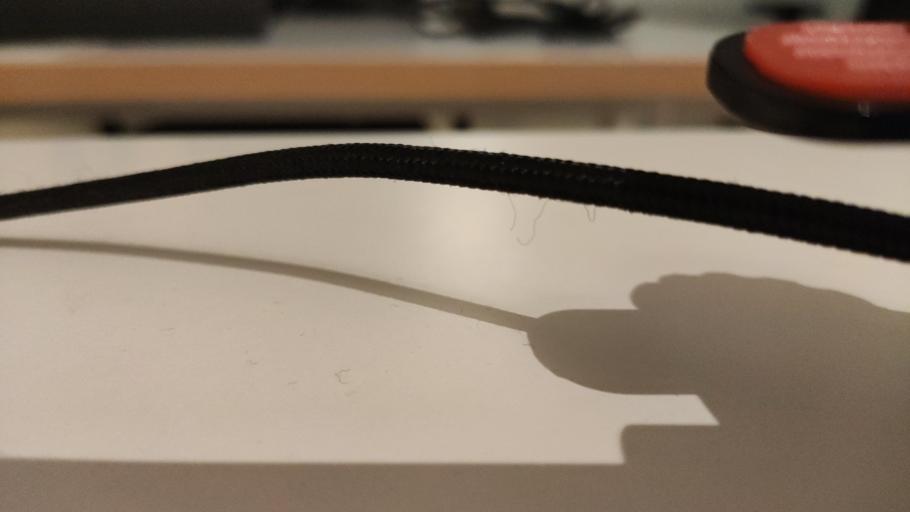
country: RU
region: Moskovskaya
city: Novoye
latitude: 55.6439
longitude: 38.9292
